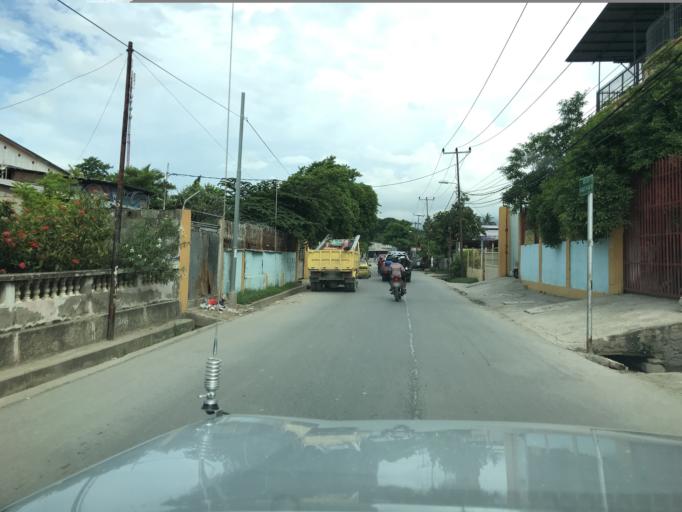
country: TL
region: Dili
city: Dili
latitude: -8.5605
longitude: 125.5603
